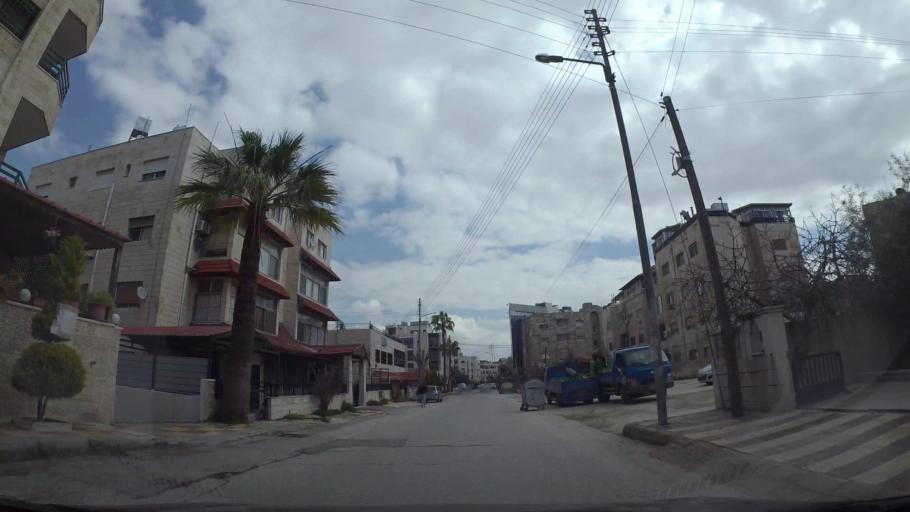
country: JO
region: Amman
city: Amman
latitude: 31.9794
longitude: 35.8965
